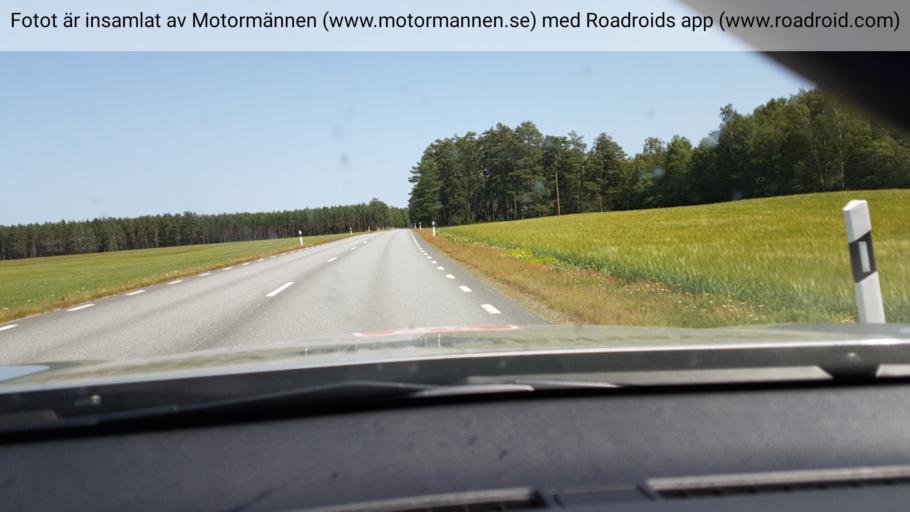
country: SE
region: Joenkoeping
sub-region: Nassjo Kommun
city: Bodafors
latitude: 57.4703
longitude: 14.7623
